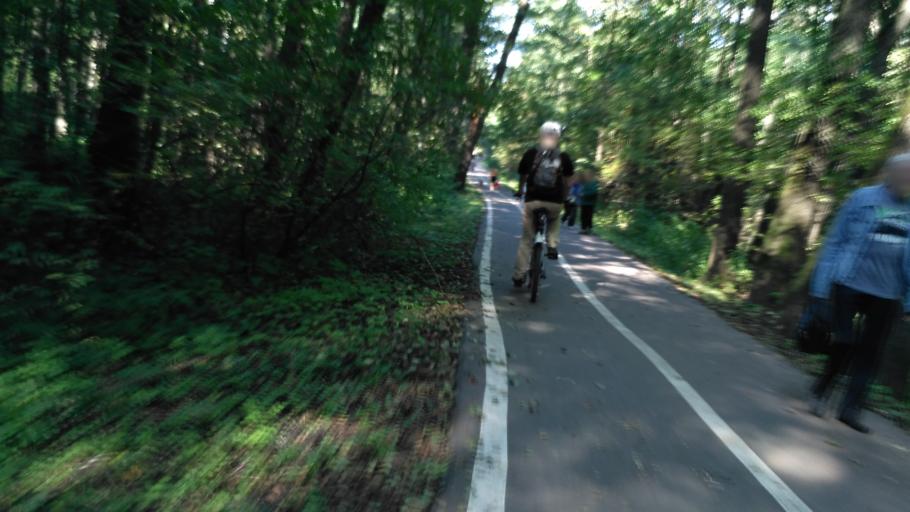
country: RU
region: Moskovskaya
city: Izmaylovo
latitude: 55.7766
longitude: 37.7747
